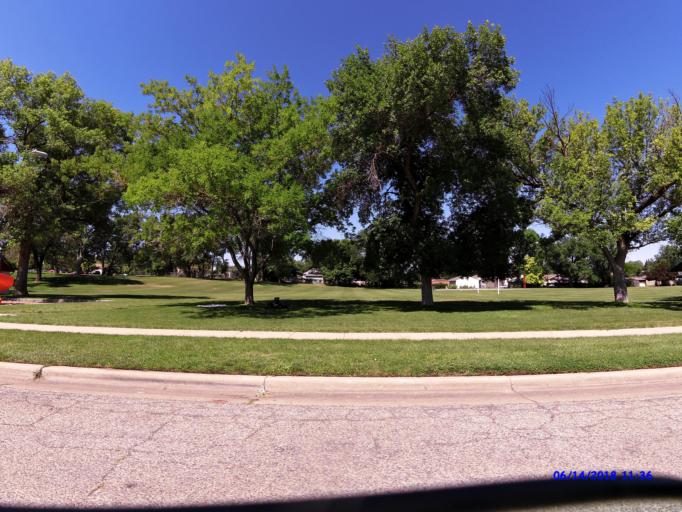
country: US
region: Utah
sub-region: Weber County
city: Ogden
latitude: 41.2218
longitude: -111.9955
